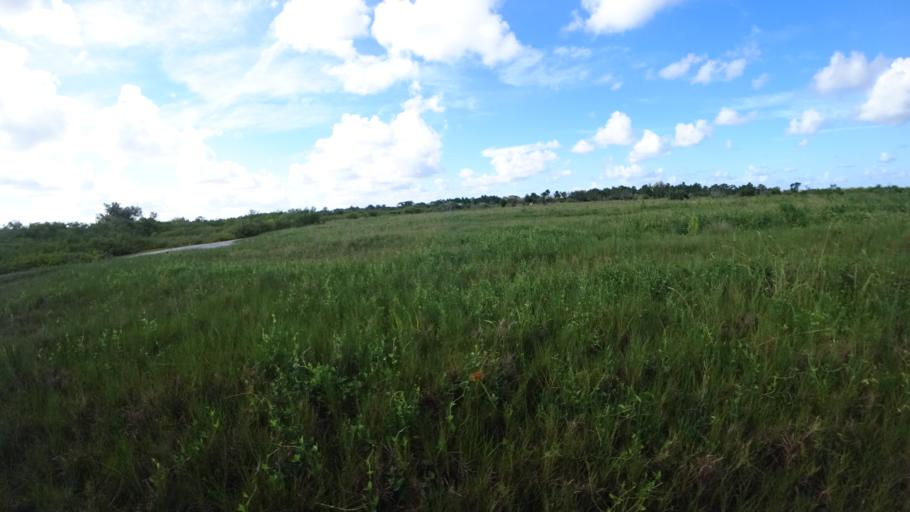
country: US
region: Florida
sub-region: Manatee County
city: West Bradenton
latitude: 27.5190
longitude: -82.6637
